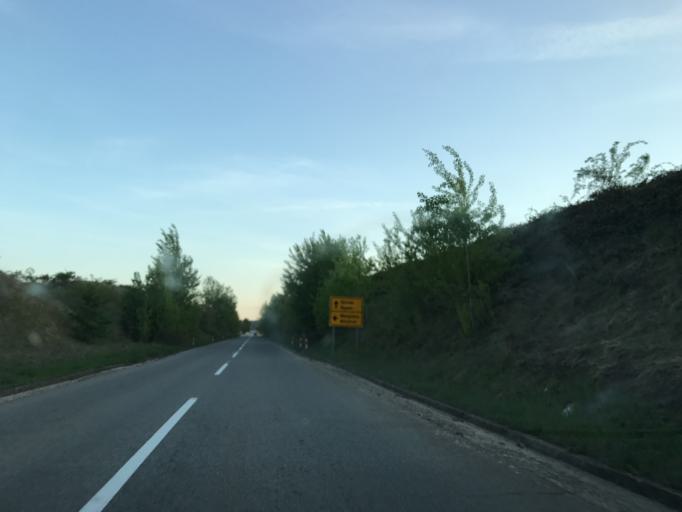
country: RO
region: Mehedinti
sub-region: Comuna Gogosu
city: Ostrovu Mare
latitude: 44.3545
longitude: 22.4773
